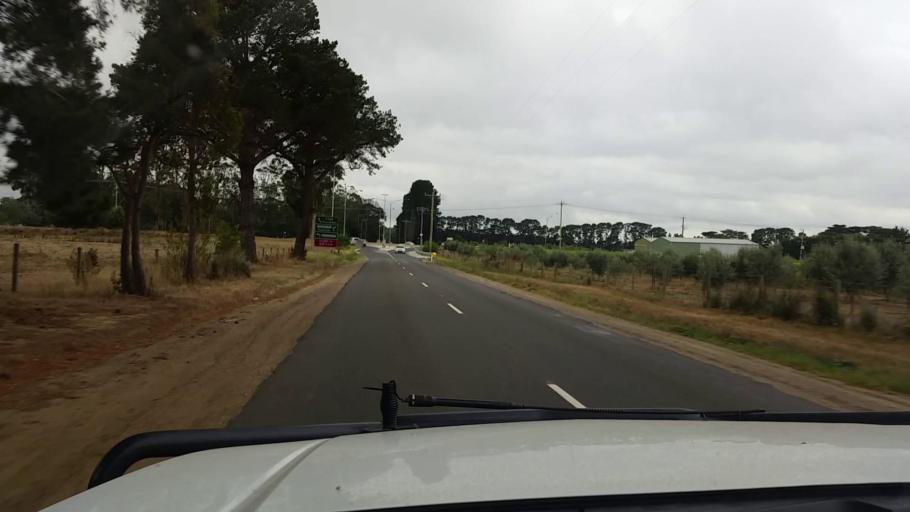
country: AU
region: Victoria
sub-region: Mornington Peninsula
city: Hastings
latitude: -38.3022
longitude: 145.1456
